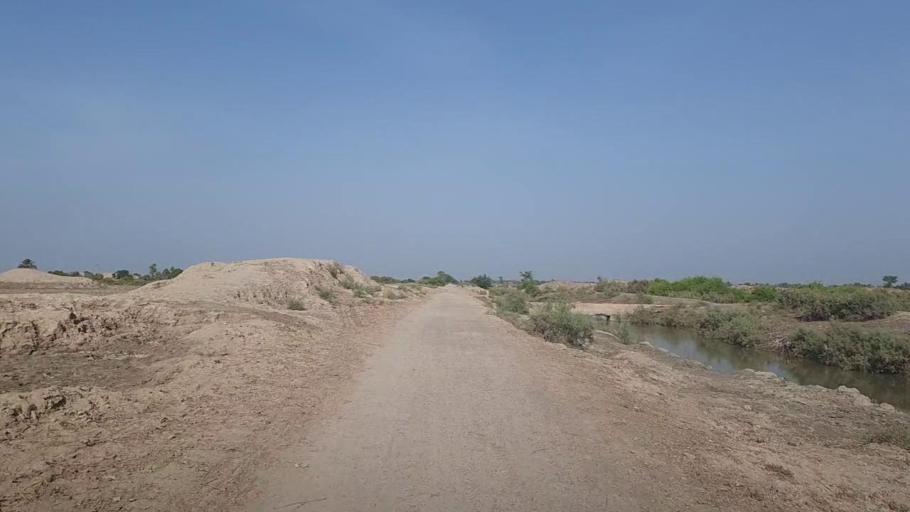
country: PK
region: Sindh
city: Sita Road
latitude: 27.0929
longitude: 67.8623
